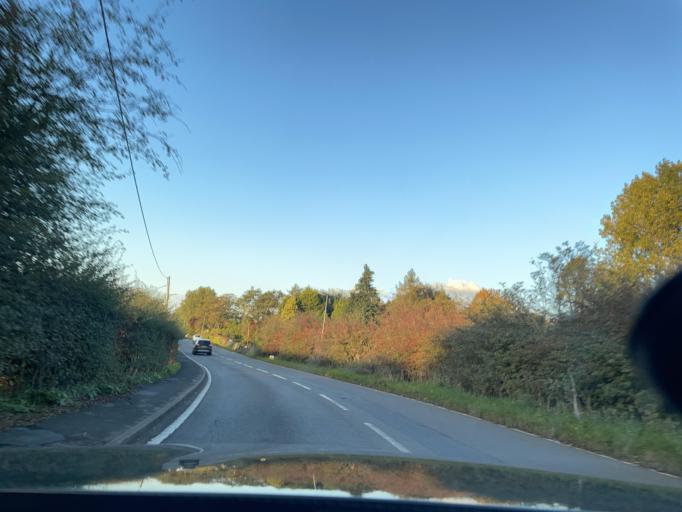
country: GB
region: England
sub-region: Borough of Tameside
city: Longdendale
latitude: 53.4363
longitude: -1.9892
